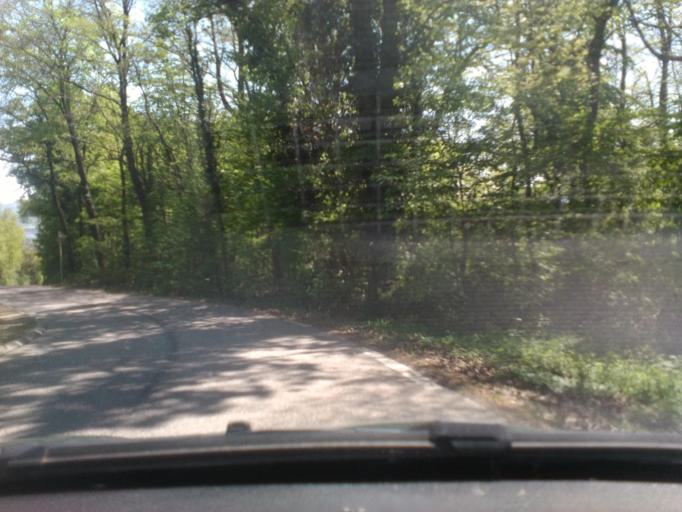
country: FR
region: Lorraine
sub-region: Departement de Meurthe-et-Moselle
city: Ludres
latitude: 48.6282
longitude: 6.1588
